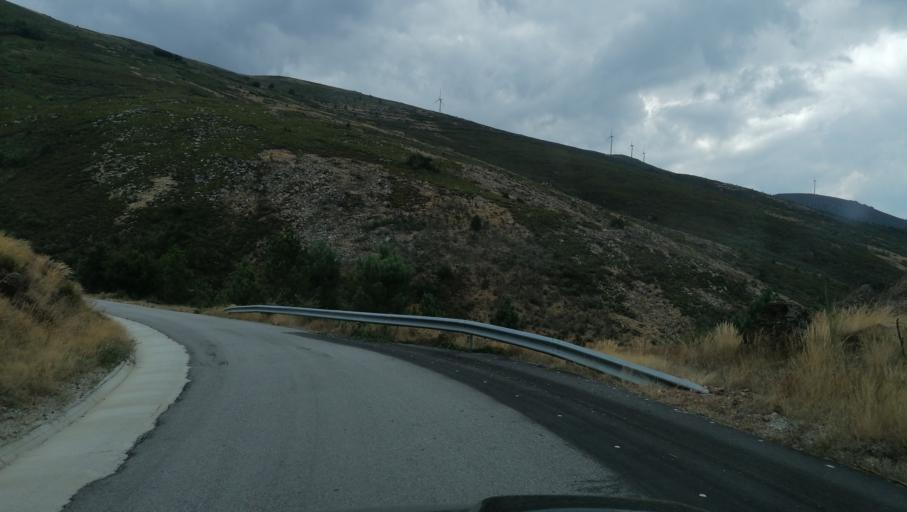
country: PT
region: Vila Real
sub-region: Vila Pouca de Aguiar
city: Vila Pouca de Aguiar
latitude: 41.5581
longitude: -7.7016
